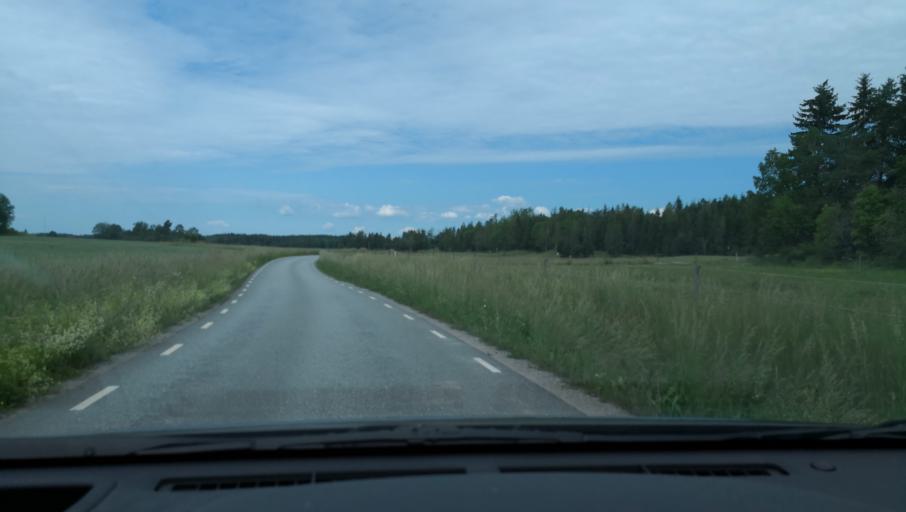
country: SE
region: Uppsala
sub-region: Habo Kommun
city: Balsta
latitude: 59.6972
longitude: 17.4803
